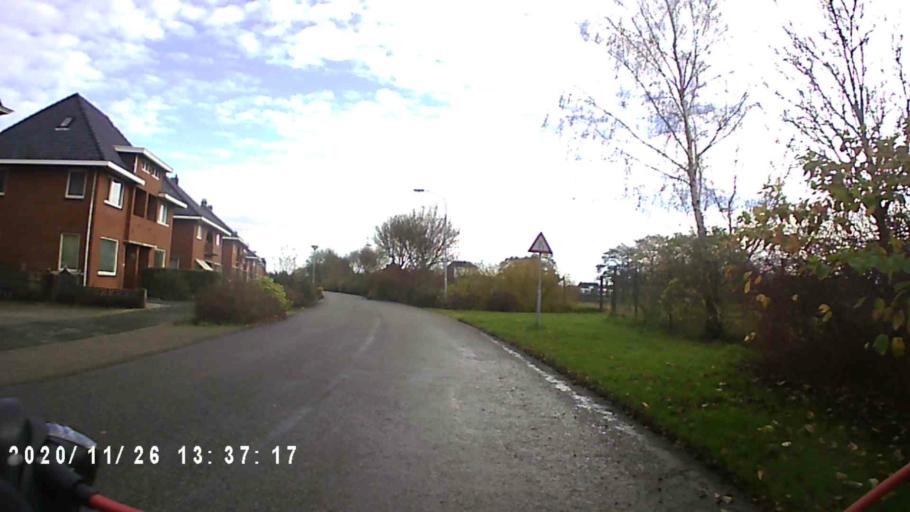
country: NL
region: Groningen
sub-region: Gemeente Delfzijl
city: Delfzijl
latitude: 53.3341
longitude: 6.9205
